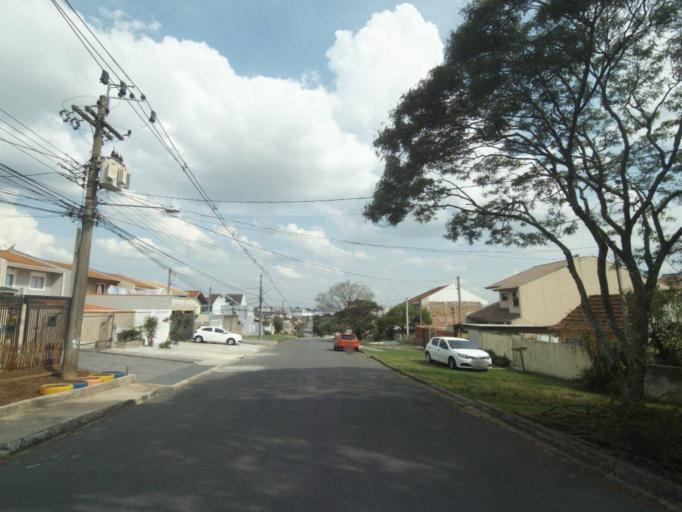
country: BR
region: Parana
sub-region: Pinhais
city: Pinhais
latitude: -25.4204
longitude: -49.2039
